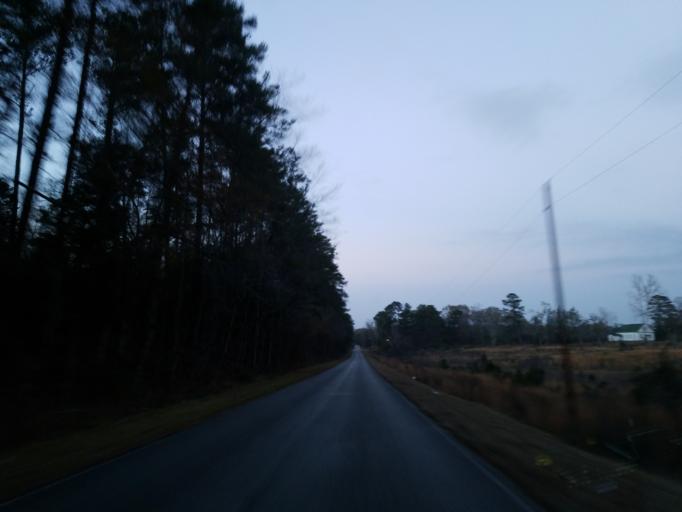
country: US
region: Alabama
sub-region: Sumter County
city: York
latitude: 32.4176
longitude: -88.4383
